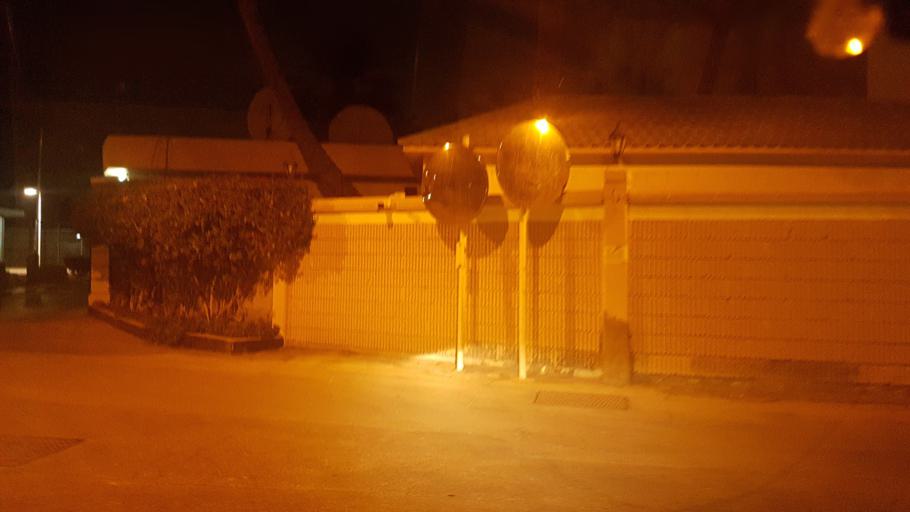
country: BH
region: Manama
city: Jidd Hafs
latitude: 26.2227
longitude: 50.4950
